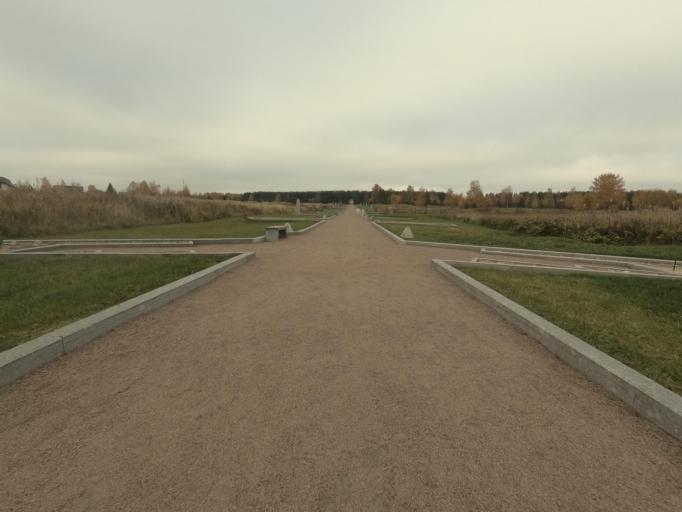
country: RU
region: Leningrad
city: Kirovsk
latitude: 59.8465
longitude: 30.9503
